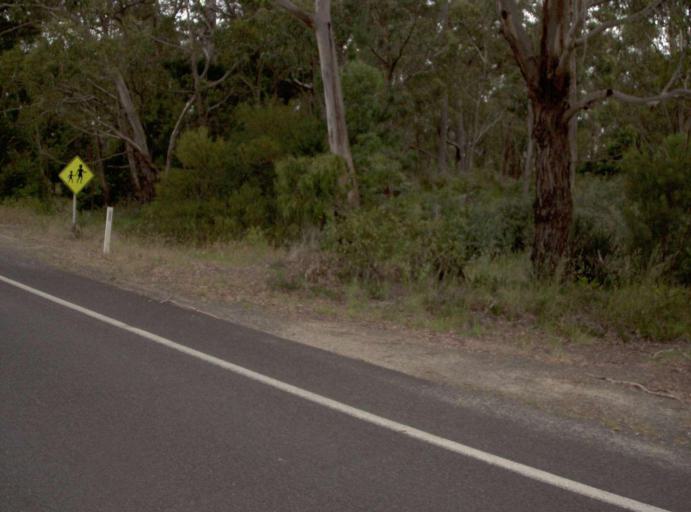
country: AU
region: Victoria
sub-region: Wellington
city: Sale
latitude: -38.5262
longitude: 146.8708
